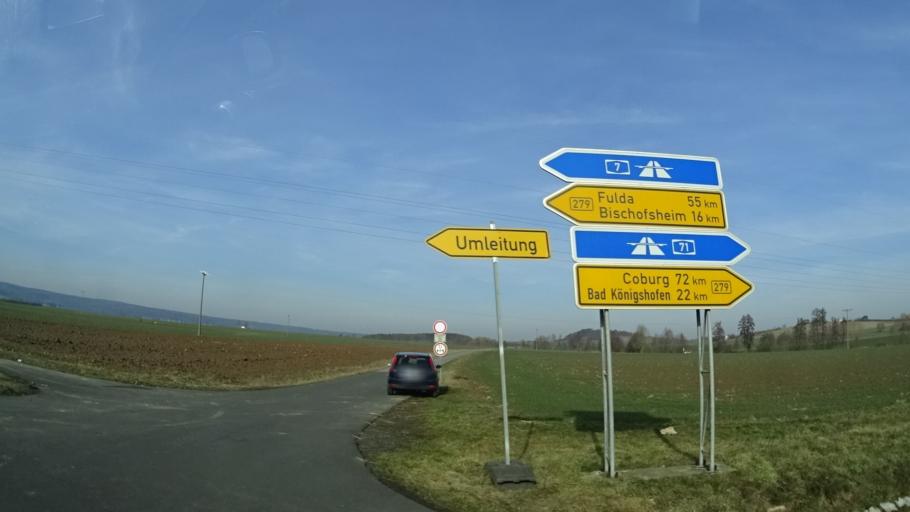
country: DE
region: Bavaria
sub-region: Regierungsbezirk Unterfranken
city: Hohenroth
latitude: 50.3387
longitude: 10.1900
